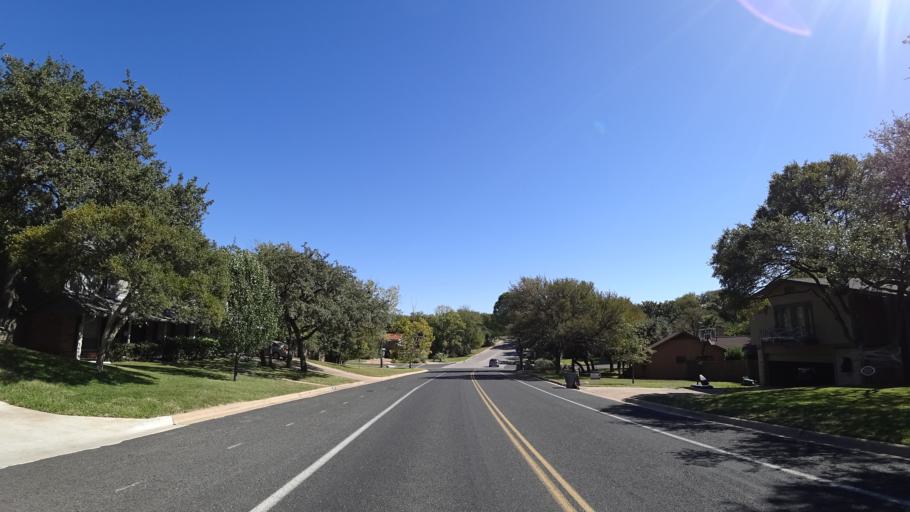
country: US
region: Texas
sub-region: Travis County
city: West Lake Hills
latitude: 30.3616
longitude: -97.7583
